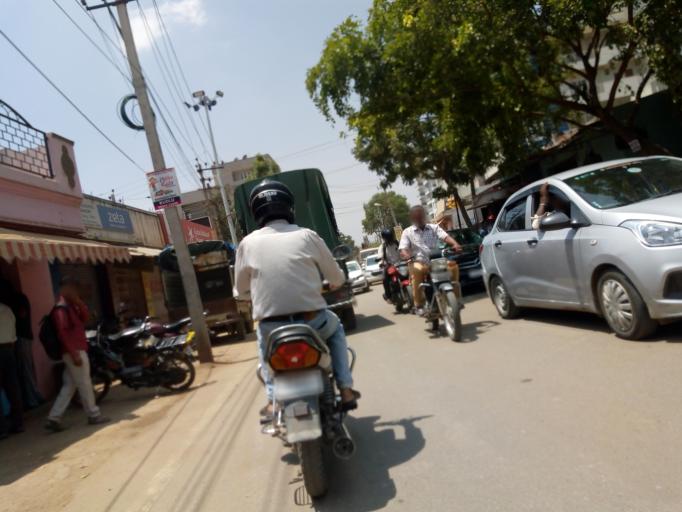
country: IN
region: Karnataka
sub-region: Bangalore Urban
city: Bangalore
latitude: 12.8874
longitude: 77.6563
